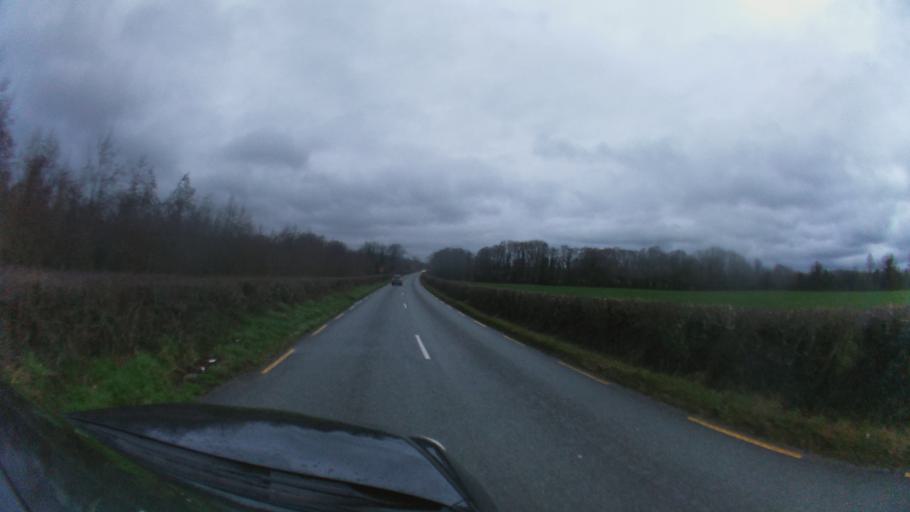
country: IE
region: Leinster
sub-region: Kilkenny
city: Graiguenamanagh
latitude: 52.5671
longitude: -6.9525
